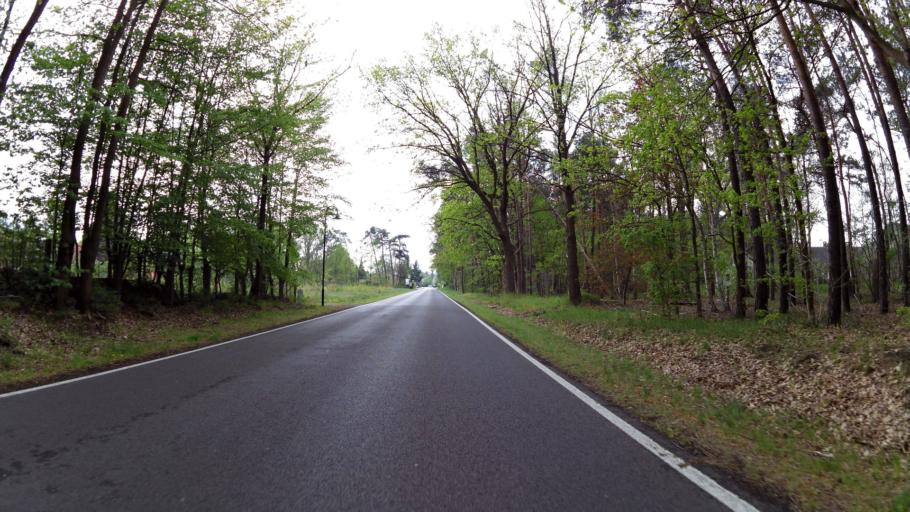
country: DE
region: Brandenburg
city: Bestensee
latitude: 52.2607
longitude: 13.7333
